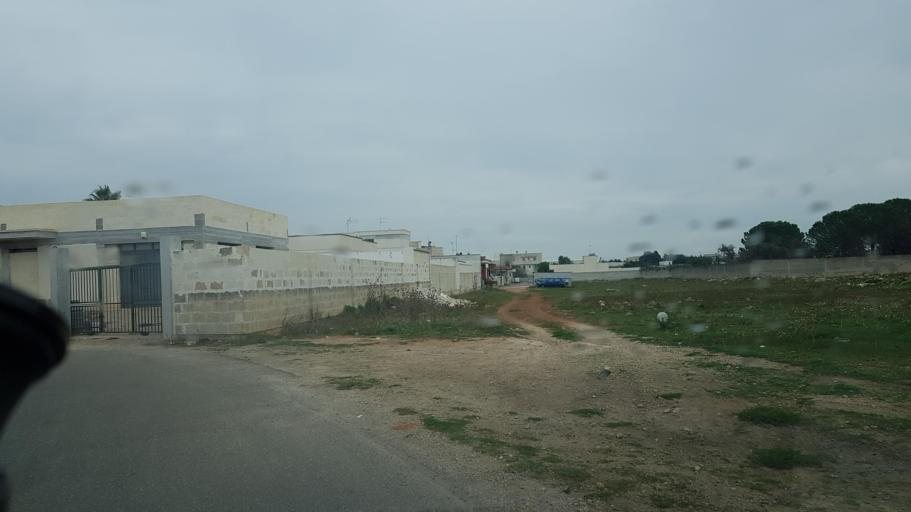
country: IT
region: Apulia
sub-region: Provincia di Lecce
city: Leverano
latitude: 40.2790
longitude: 17.9873
